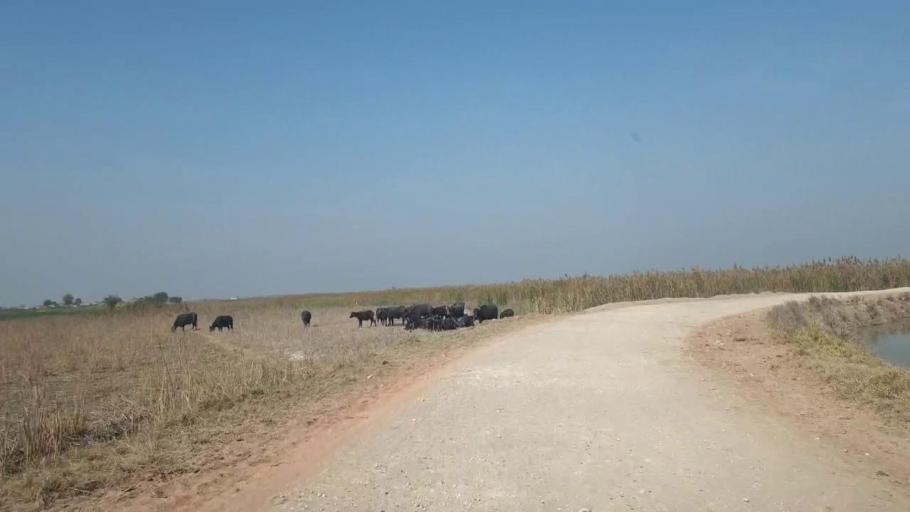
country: PK
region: Sindh
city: Sakrand
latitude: 26.0659
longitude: 68.4110
